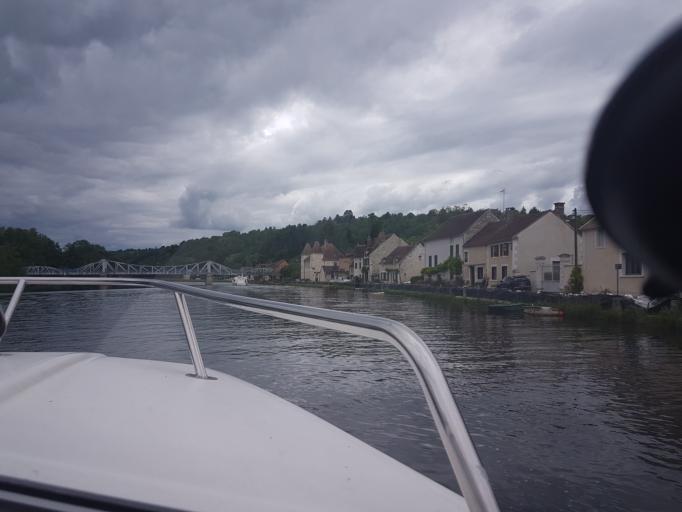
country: FR
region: Bourgogne
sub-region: Departement de l'Yonne
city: Augy
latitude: 47.7560
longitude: 3.5925
